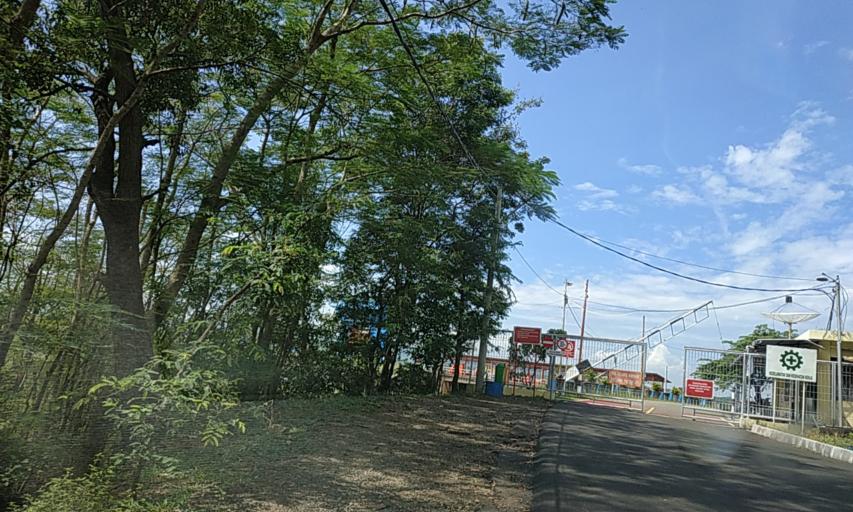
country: ID
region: Central Java
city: Selogiri
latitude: -7.8380
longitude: 110.9249
